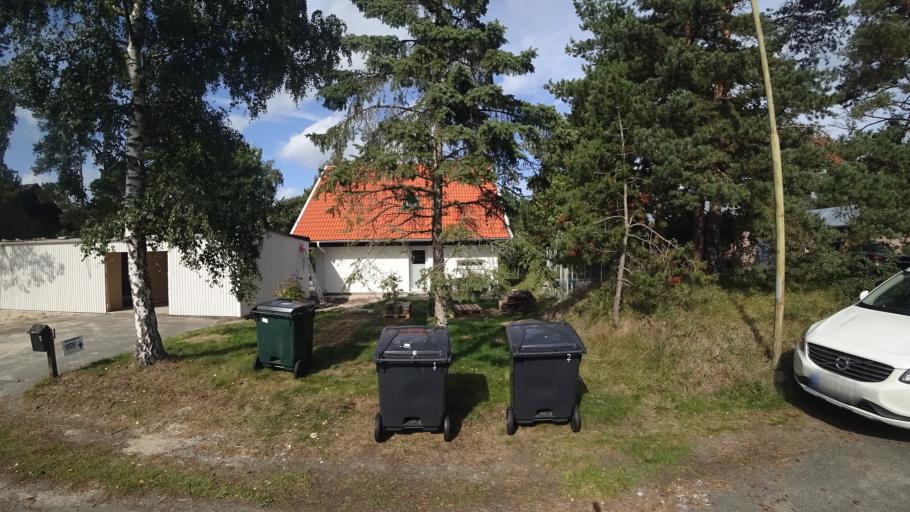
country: SE
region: Skane
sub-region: Kristianstads Kommun
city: Ahus
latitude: 55.9097
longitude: 14.2923
